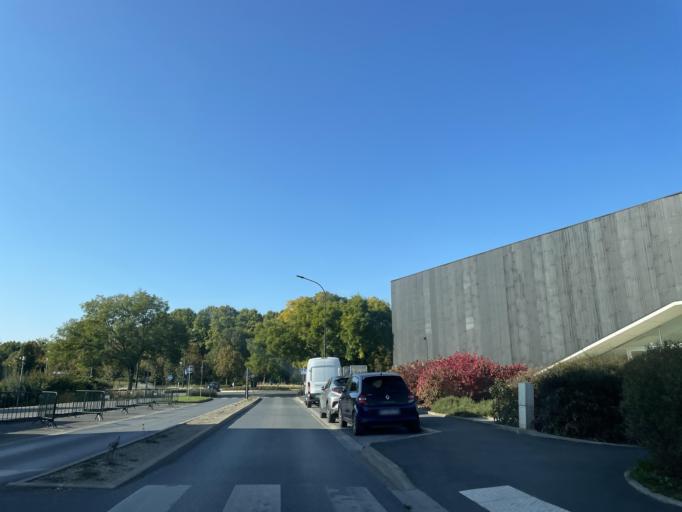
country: FR
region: Ile-de-France
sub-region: Departement de Seine-et-Marne
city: Coulommiers
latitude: 48.8090
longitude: 3.0909
